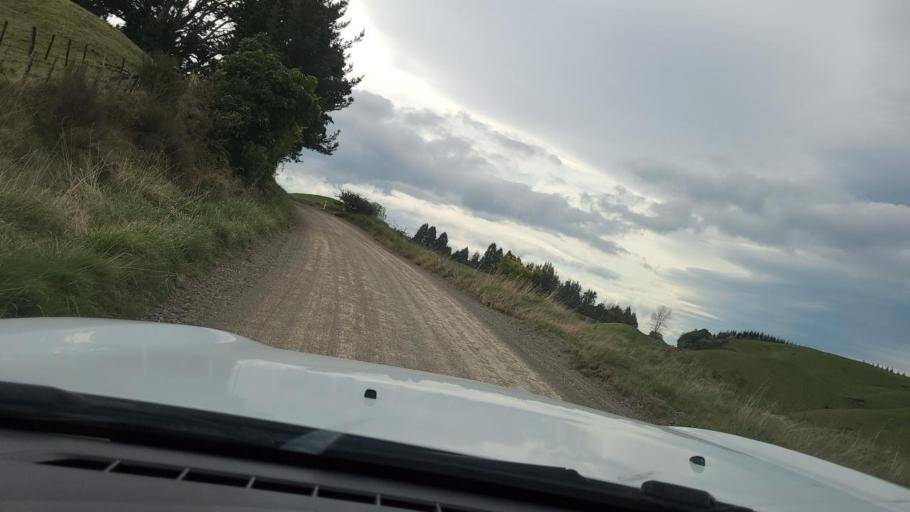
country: NZ
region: Hawke's Bay
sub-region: Napier City
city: Napier
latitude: -39.2630
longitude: 176.8430
